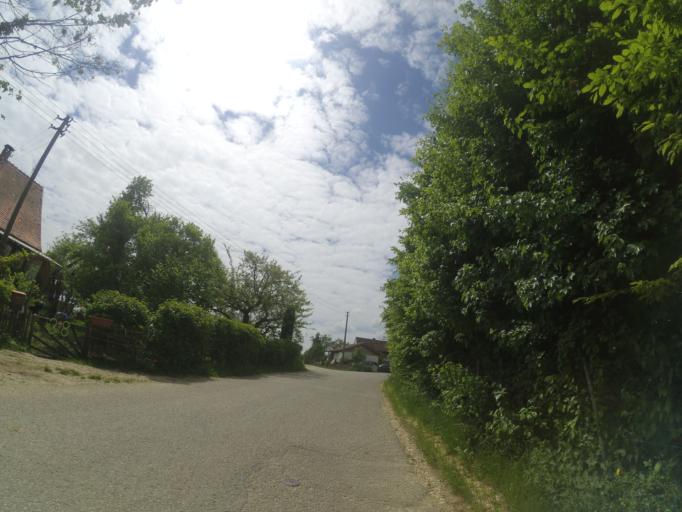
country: DE
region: Baden-Wuerttemberg
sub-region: Tuebingen Region
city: Blaubeuren
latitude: 48.4334
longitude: 9.7744
